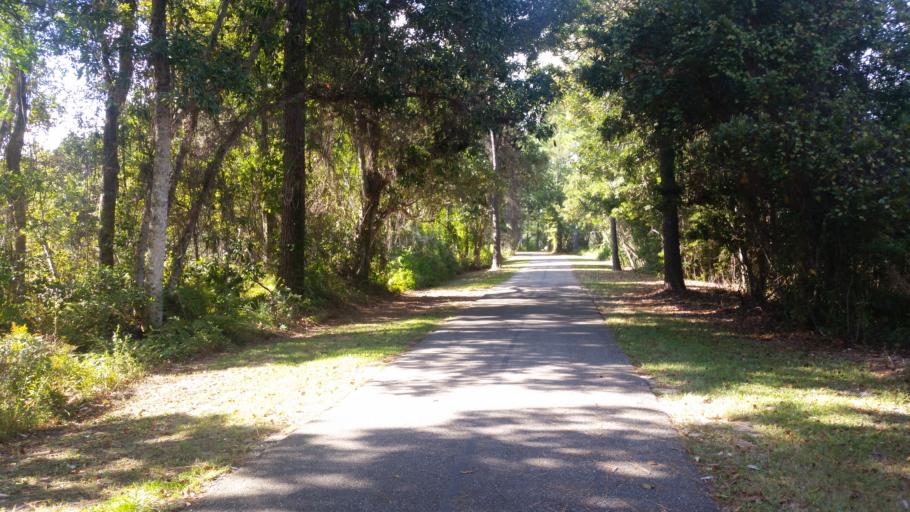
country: US
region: Alabama
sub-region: Baldwin County
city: Orange Beach
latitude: 30.2755
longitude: -87.6075
